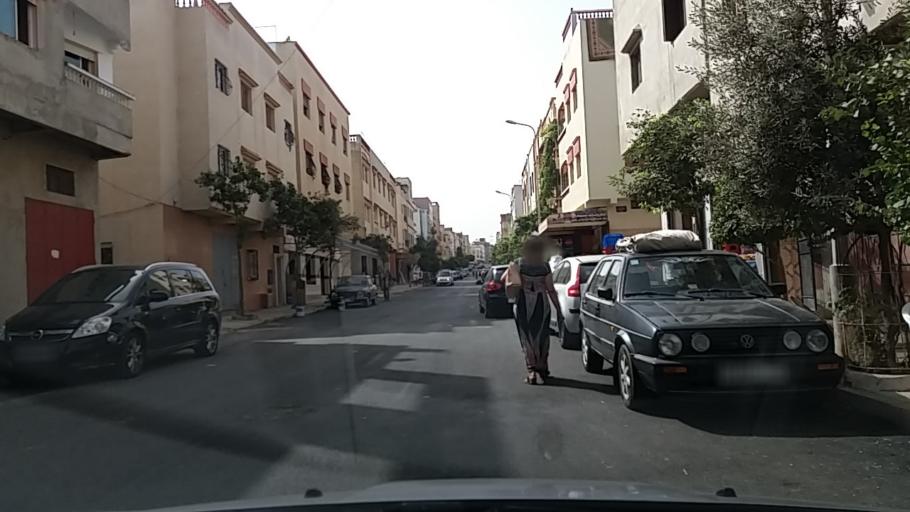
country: MA
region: Tanger-Tetouan
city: Asilah
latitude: 35.4595
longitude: -6.0387
